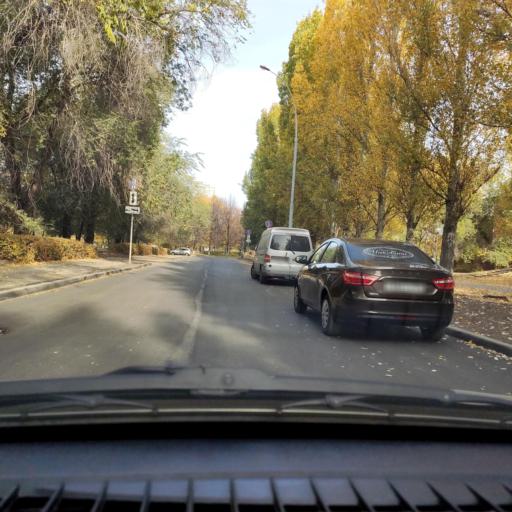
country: RU
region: Samara
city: Tol'yatti
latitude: 53.5244
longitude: 49.3021
